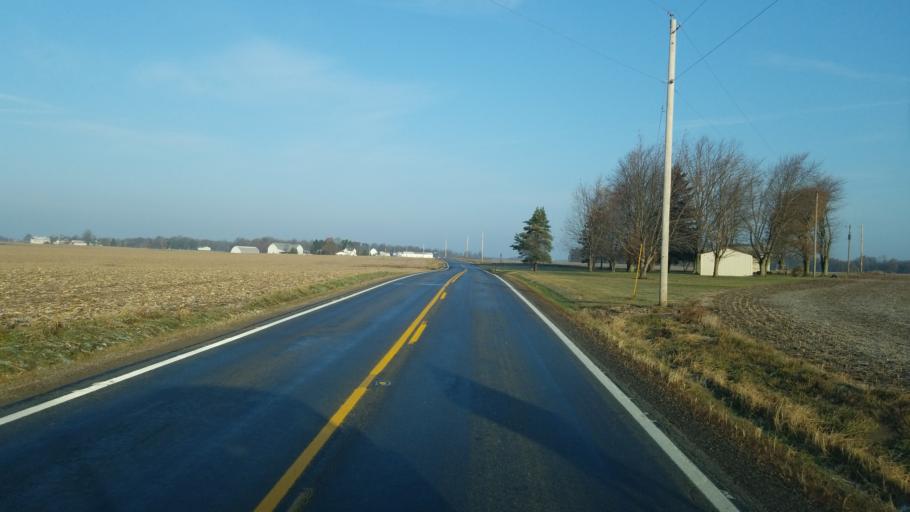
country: US
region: Ohio
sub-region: Crawford County
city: Bucyrus
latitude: 40.7557
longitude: -82.9102
